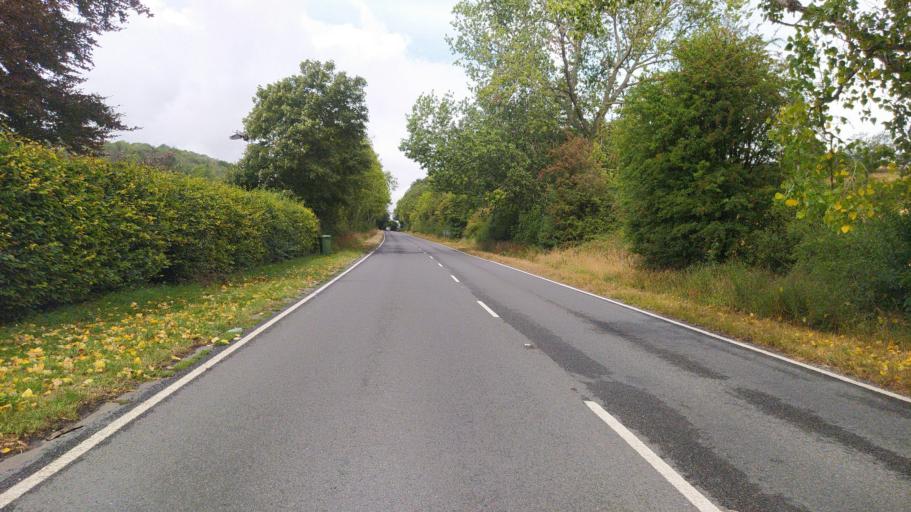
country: GB
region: England
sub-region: Hampshire
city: Petersfield
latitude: 50.9714
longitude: -0.8899
